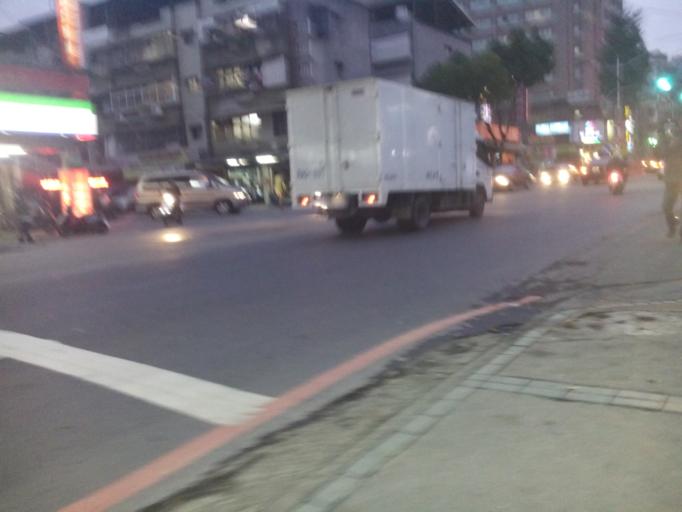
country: TW
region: Taipei
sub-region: Taipei
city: Banqiao
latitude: 24.9814
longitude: 121.4210
